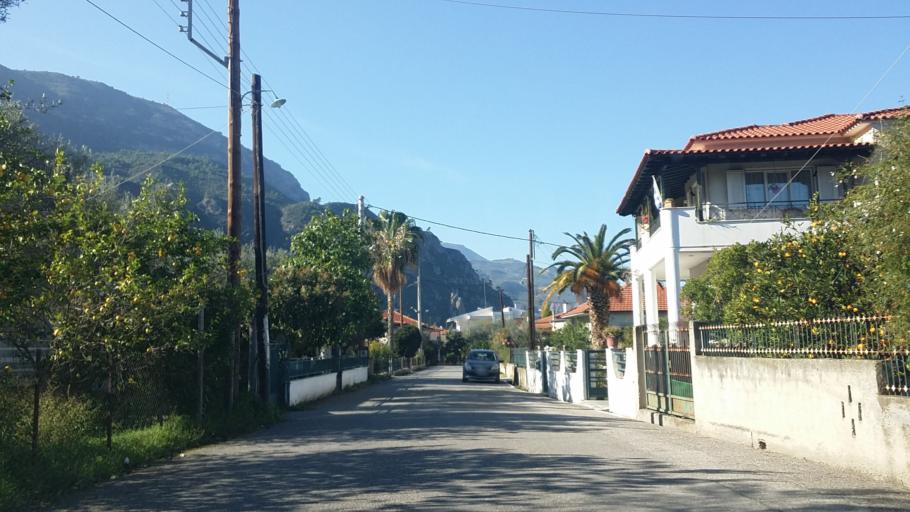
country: GR
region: West Greece
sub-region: Nomos Achaias
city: Temeni
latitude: 38.1869
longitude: 22.1868
